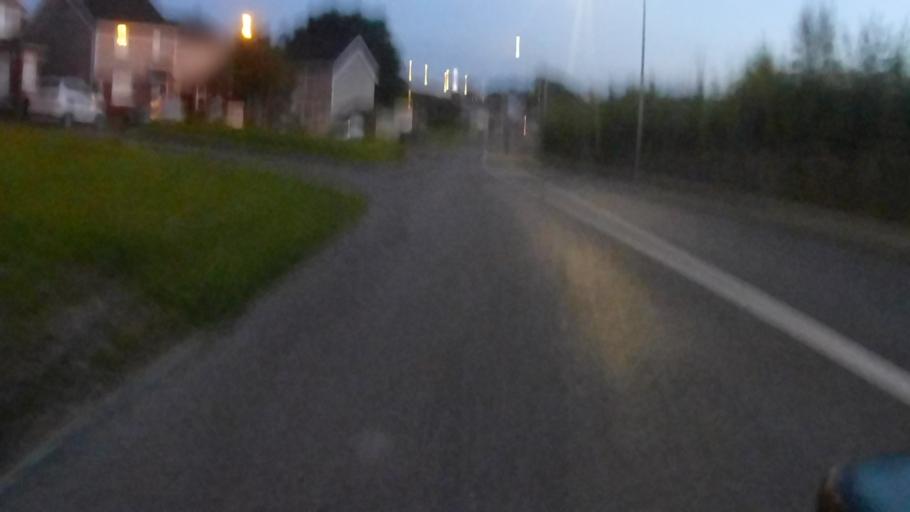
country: IE
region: Munster
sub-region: County Cork
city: Cork
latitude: 51.9168
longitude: -8.4252
